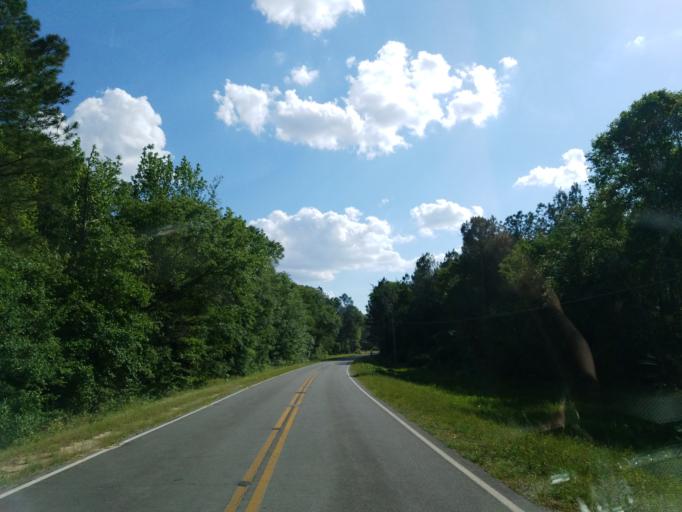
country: US
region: Georgia
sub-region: Crisp County
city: Cordele
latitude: 32.0000
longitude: -83.7462
